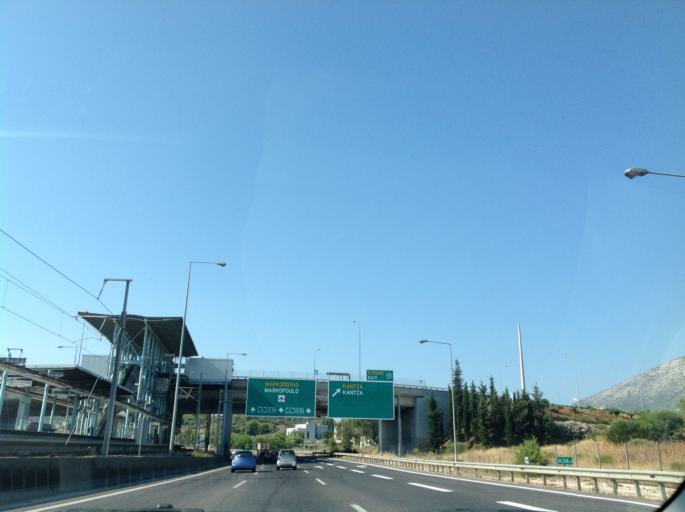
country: GR
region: Attica
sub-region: Nomarchia Anatolikis Attikis
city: Pallini
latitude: 37.9852
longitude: 23.8700
